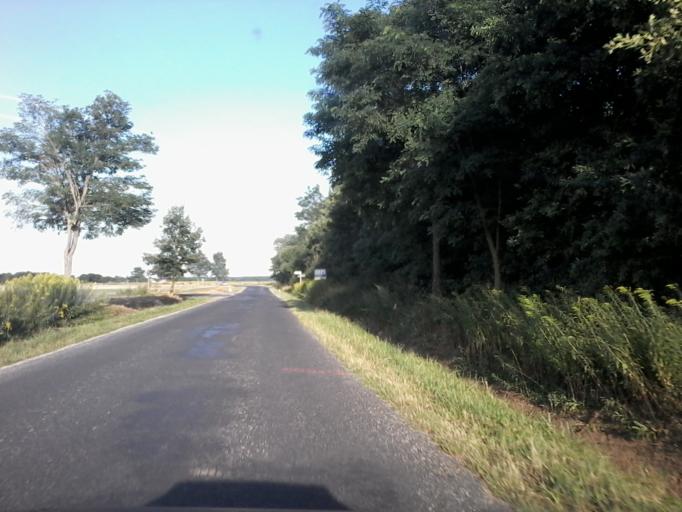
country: HU
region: Vas
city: Celldomolk
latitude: 47.2066
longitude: 17.0932
